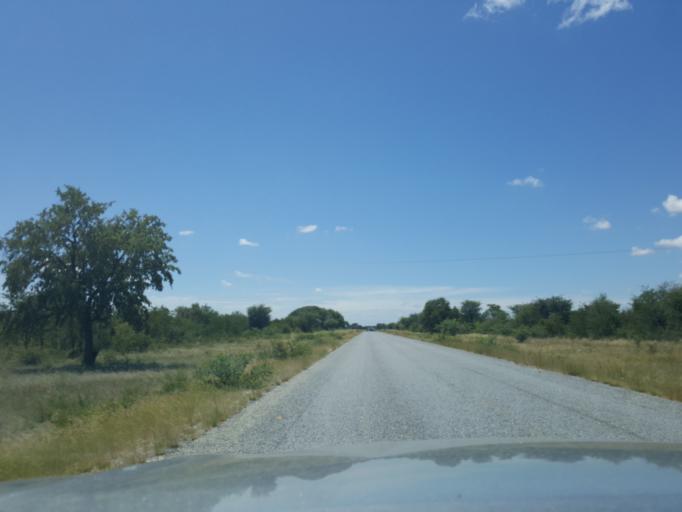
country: BW
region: Central
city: Nata
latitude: -20.1508
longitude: 25.7684
